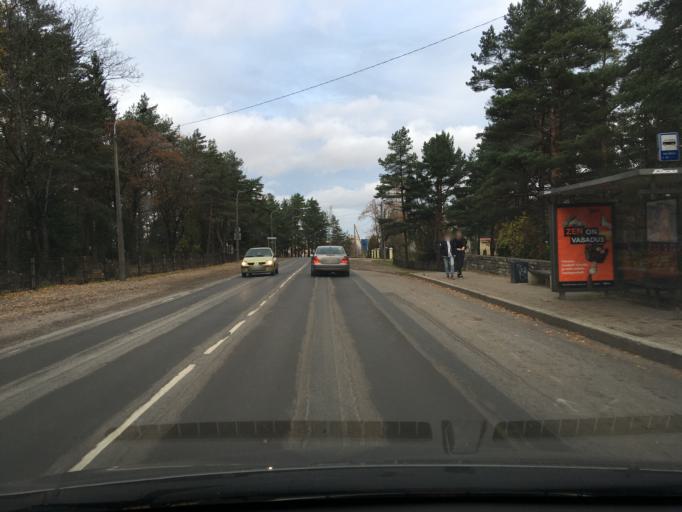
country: EE
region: Harju
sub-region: Tallinna linn
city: Tallinn
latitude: 59.3923
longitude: 24.7085
